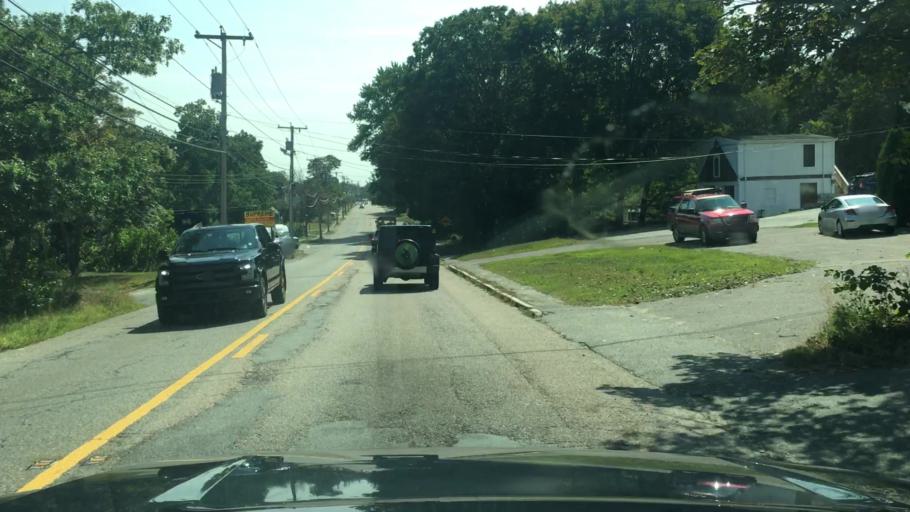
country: US
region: Massachusetts
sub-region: Plymouth County
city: Abington
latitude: 42.1351
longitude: -70.9503
